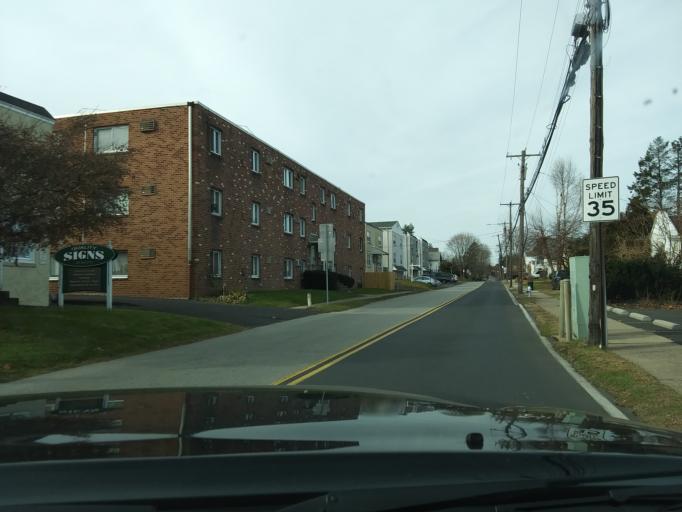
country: US
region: Pennsylvania
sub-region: Montgomery County
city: Rockledge
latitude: 40.0846
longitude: -75.0943
